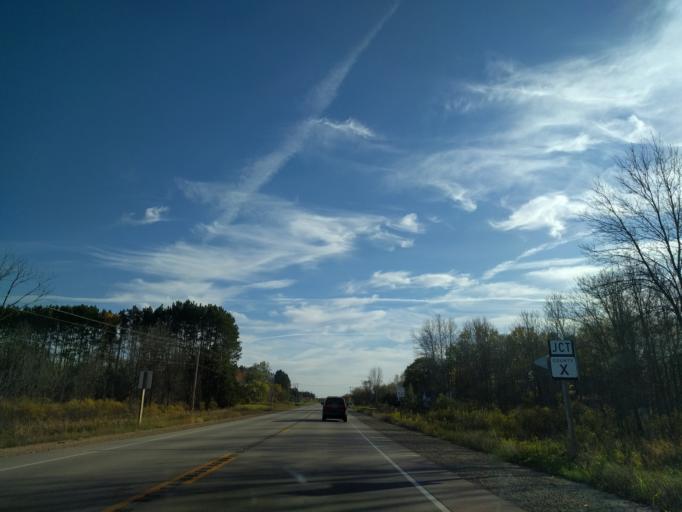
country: US
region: Wisconsin
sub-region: Marinette County
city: Peshtigo
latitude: 45.2974
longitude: -87.9919
